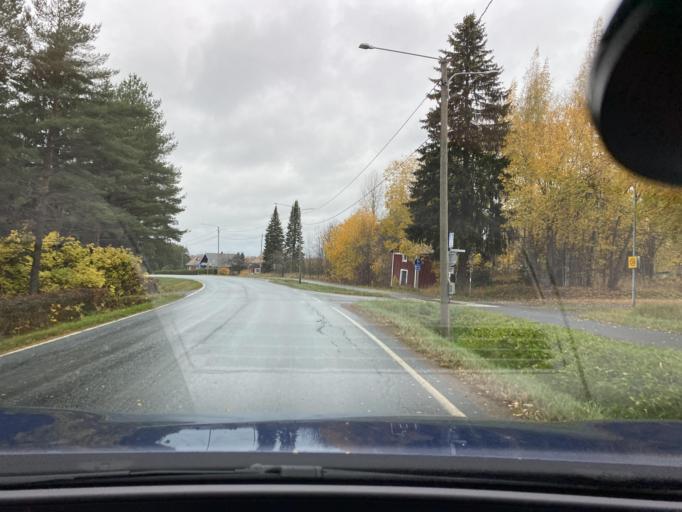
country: FI
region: Satakunta
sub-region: Pori
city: Kokemaeki
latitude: 61.2587
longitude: 22.3864
